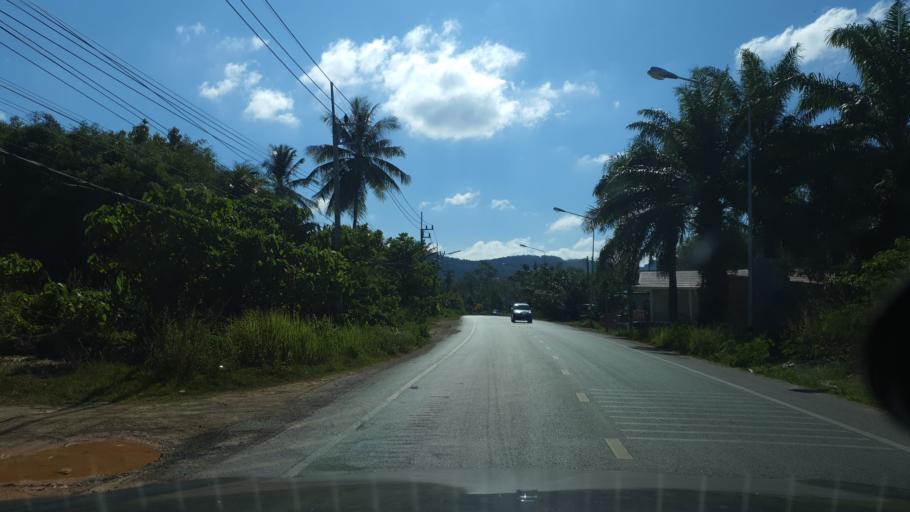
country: TH
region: Phangnga
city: Ban Ao Nang
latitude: 8.0641
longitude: 98.8107
